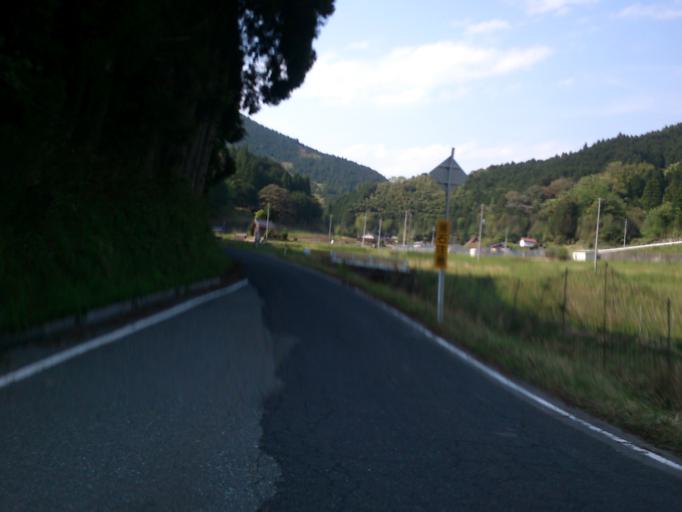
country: JP
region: Kyoto
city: Fukuchiyama
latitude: 35.3602
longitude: 135.0103
